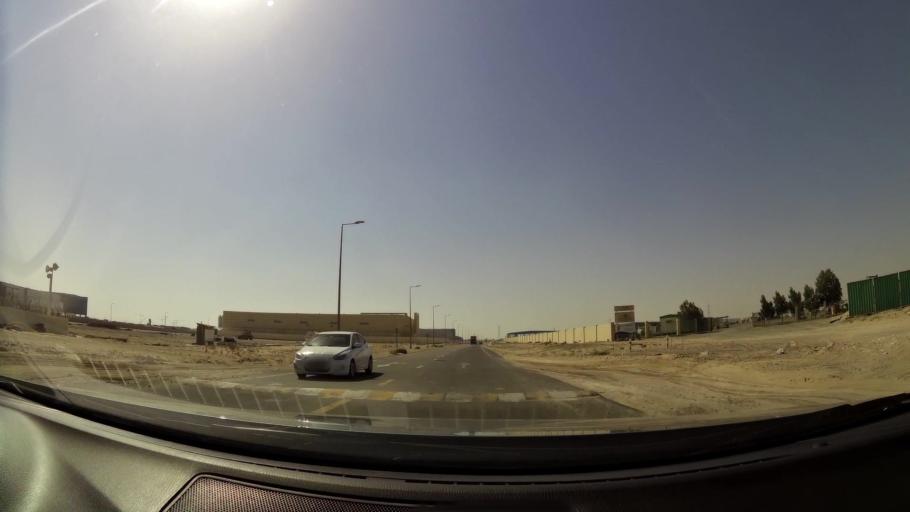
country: AE
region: Dubai
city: Dubai
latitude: 24.9160
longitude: 55.0666
